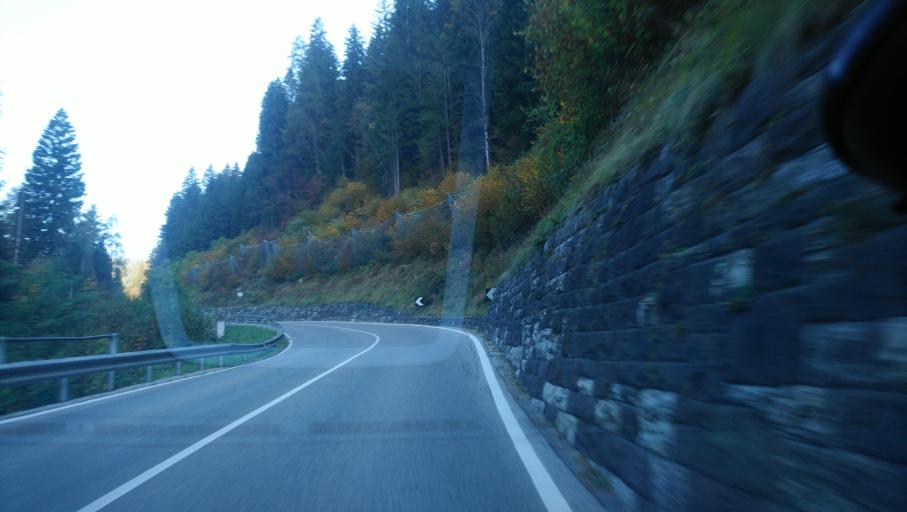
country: IT
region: Veneto
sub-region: Provincia di Belluno
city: Canale d'Agordo
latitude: 46.3631
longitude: 11.9082
